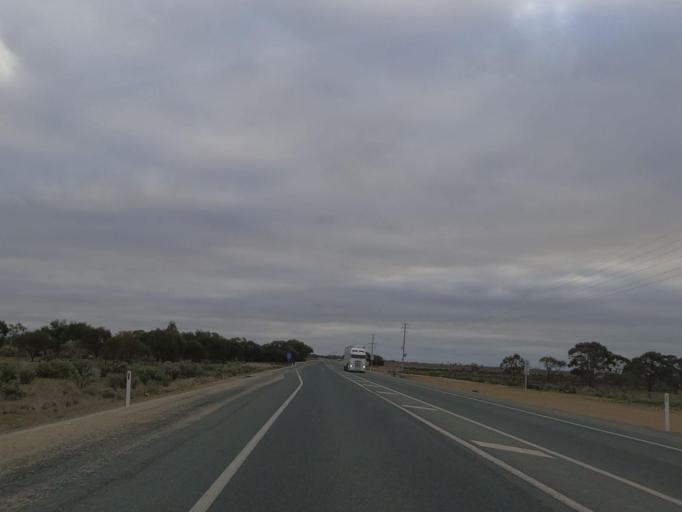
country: AU
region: Victoria
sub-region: Swan Hill
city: Swan Hill
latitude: -35.5464
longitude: 143.7613
